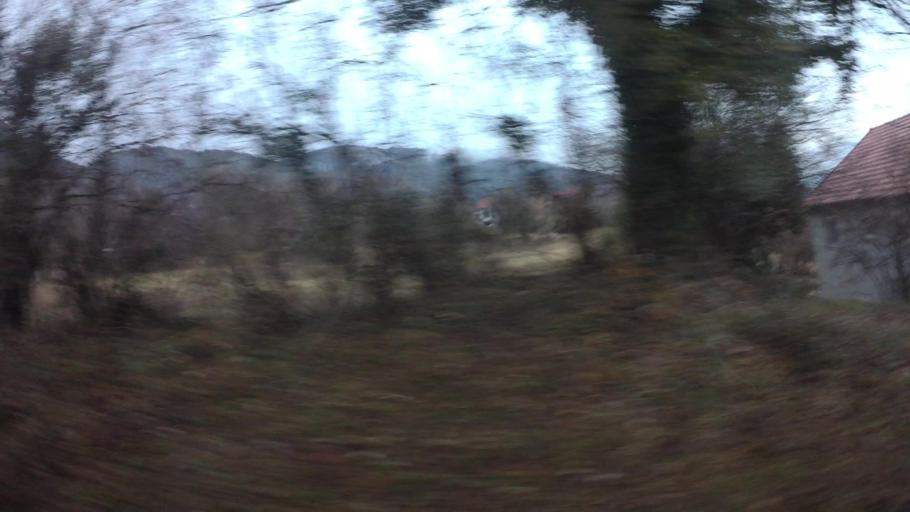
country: BA
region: Federation of Bosnia and Herzegovina
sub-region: Hercegovacko-Bosanski Kanton
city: Mostar
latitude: 43.3662
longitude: 17.8012
